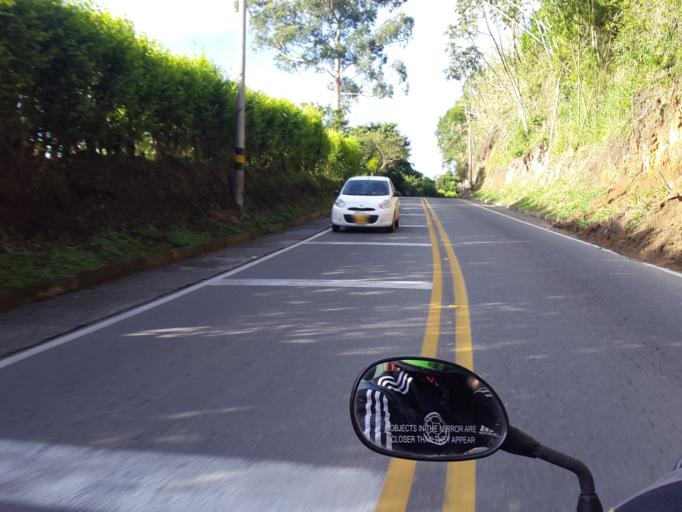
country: CO
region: Quindio
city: Montenegro
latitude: 4.5716
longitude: -75.7625
